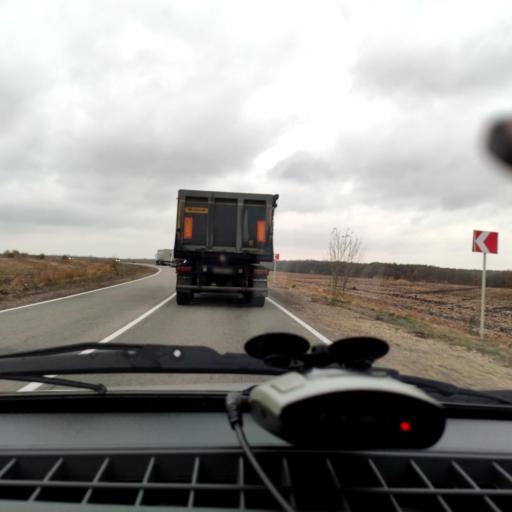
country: RU
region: Voronezj
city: Shilovo
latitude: 51.4514
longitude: 38.9879
